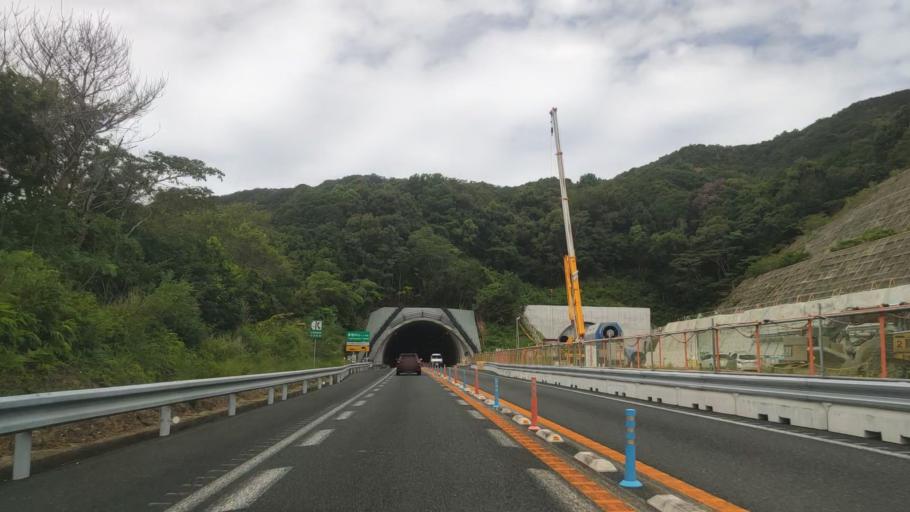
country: JP
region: Wakayama
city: Gobo
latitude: 33.8485
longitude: 135.2168
